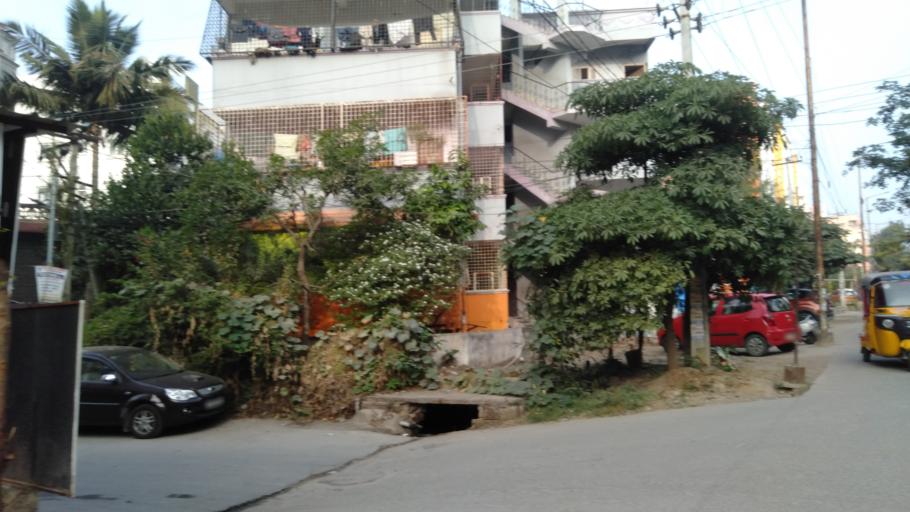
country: IN
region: Telangana
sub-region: Rangareddi
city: Kukatpalli
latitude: 17.4858
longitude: 78.3888
